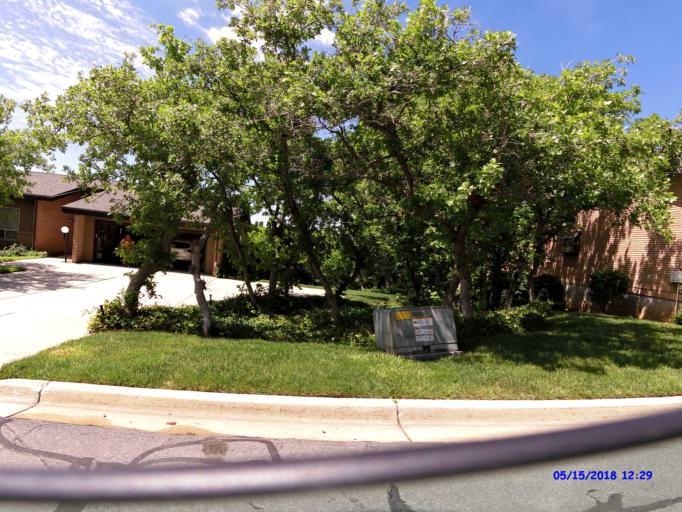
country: US
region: Utah
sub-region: Weber County
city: Uintah
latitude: 41.1745
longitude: -111.9284
